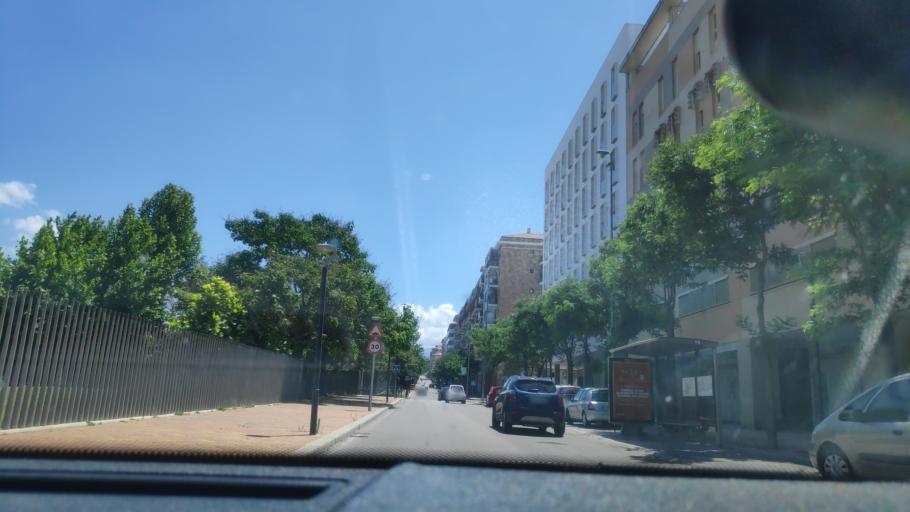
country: ES
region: Andalusia
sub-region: Provincia de Jaen
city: Jaen
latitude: 37.7888
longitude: -3.7918
